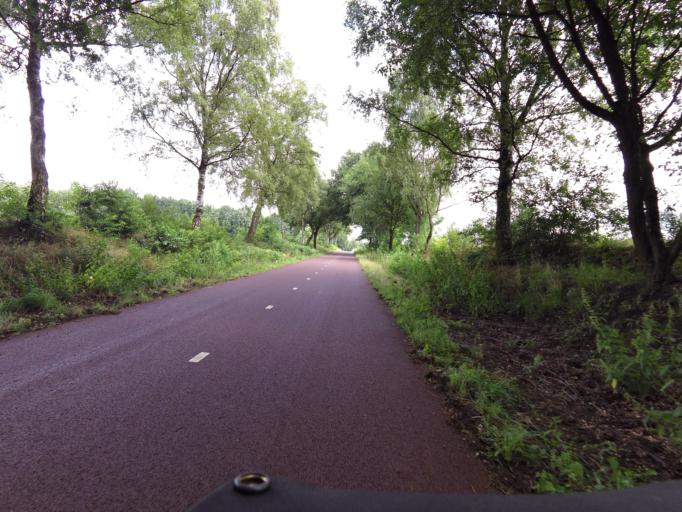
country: DE
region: North Rhine-Westphalia
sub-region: Regierungsbezirk Dusseldorf
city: Bruggen
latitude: 51.1790
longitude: 6.1444
